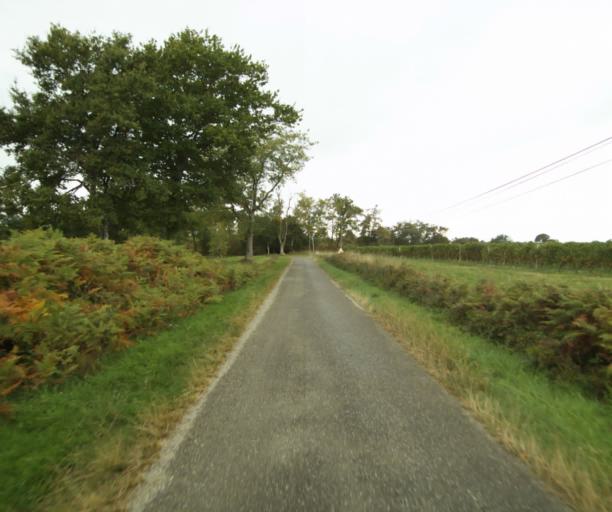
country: FR
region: Midi-Pyrenees
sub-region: Departement du Gers
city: Eauze
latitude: 43.9036
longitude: 0.0425
